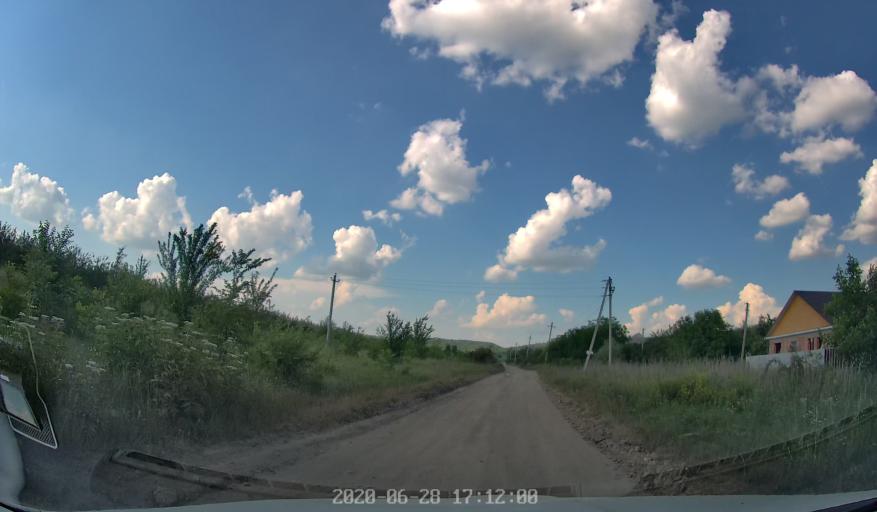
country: MD
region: Chisinau
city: Vatra
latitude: 46.9875
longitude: 28.6972
